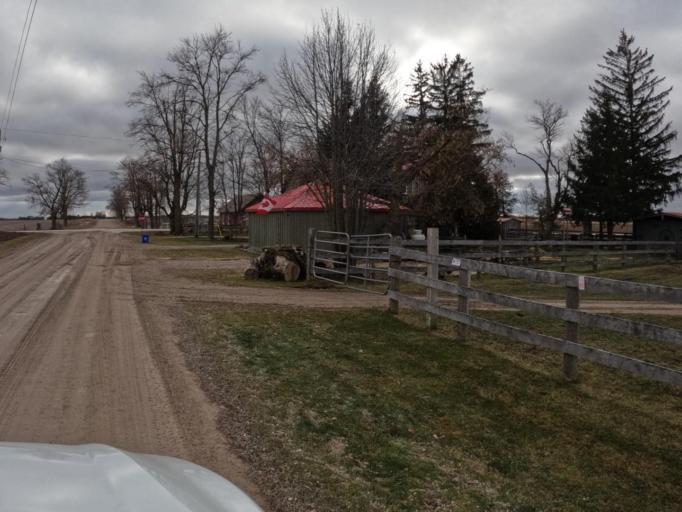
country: CA
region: Ontario
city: Shelburne
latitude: 43.8811
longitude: -80.4043
